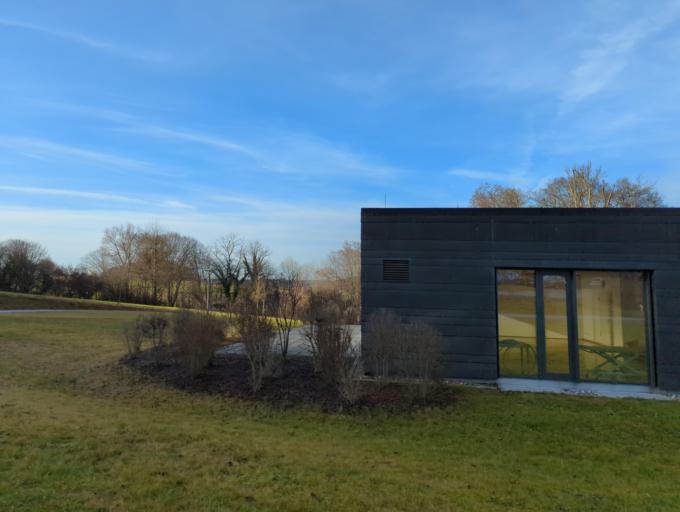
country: DE
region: Bavaria
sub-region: Swabia
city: Krumbach
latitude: 48.2454
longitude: 10.3898
